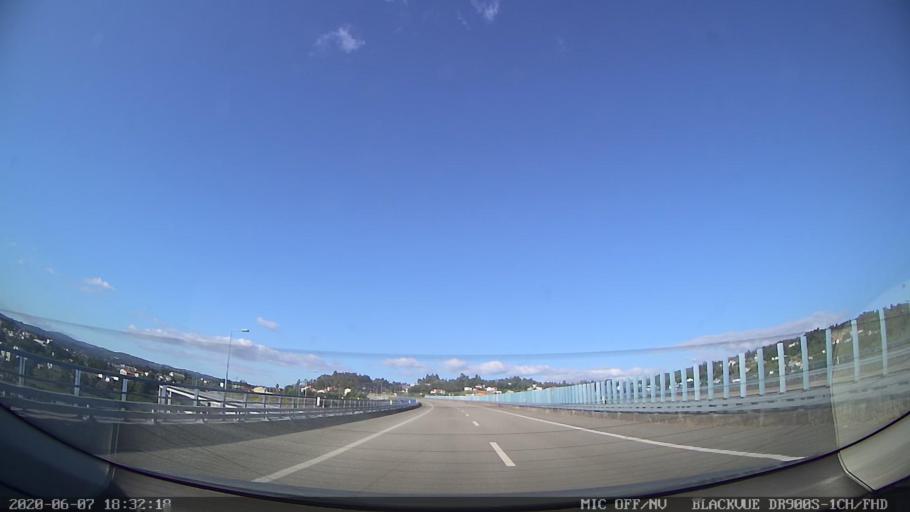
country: PT
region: Braga
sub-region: Fafe
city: Fafe
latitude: 41.4373
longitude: -8.1672
